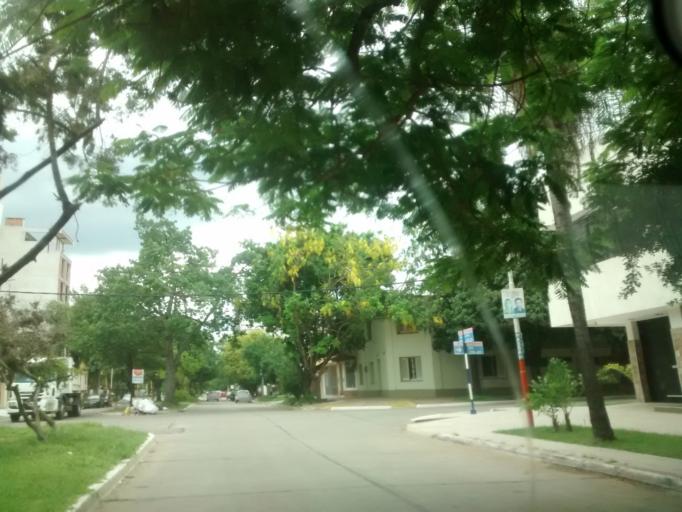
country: AR
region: Chaco
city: Resistencia
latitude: -27.4423
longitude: -58.9855
